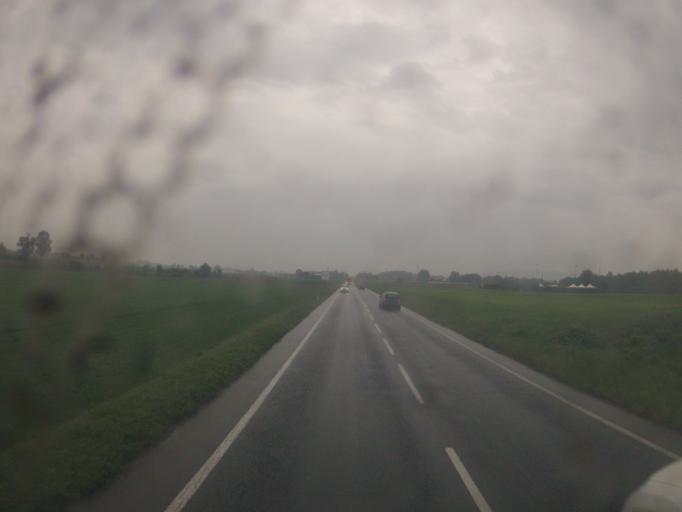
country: IT
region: Piedmont
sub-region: Provincia di Torino
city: Carignano
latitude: 44.9268
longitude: 7.6728
